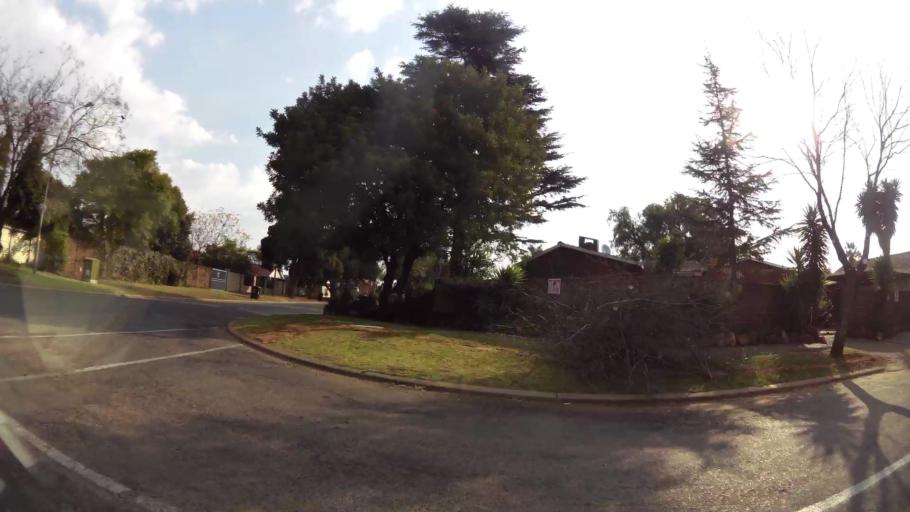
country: ZA
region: Gauteng
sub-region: City of Johannesburg Metropolitan Municipality
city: Modderfontein
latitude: -26.0973
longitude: 28.1984
